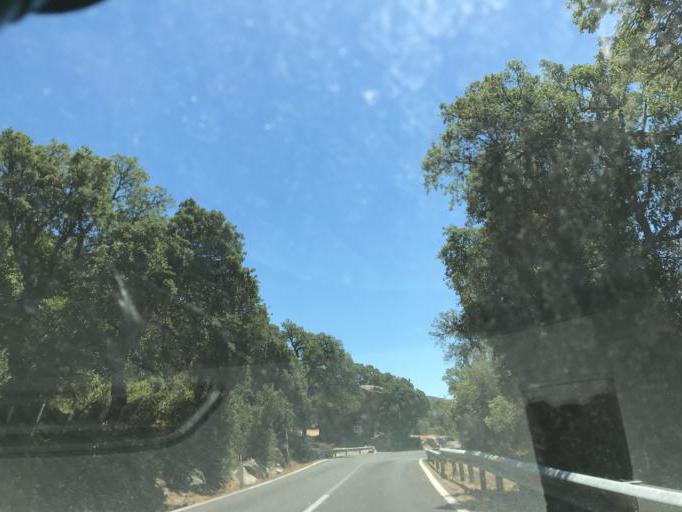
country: IT
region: Sardinia
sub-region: Provincia di Olbia-Tempio
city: Calangianus
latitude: 40.9092
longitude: 9.1965
